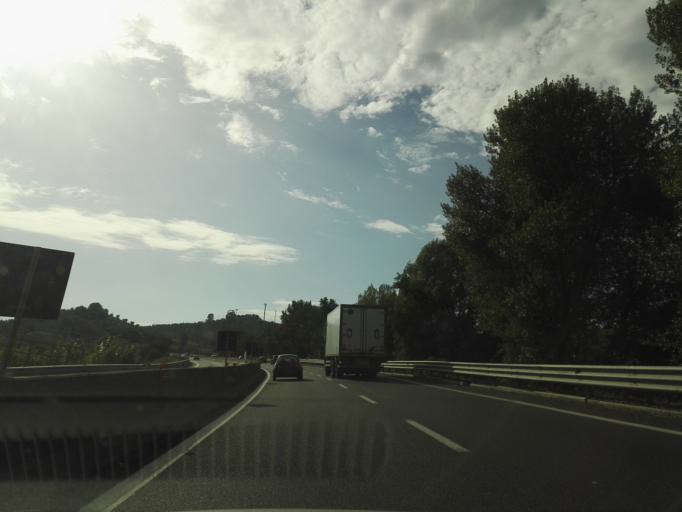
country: IT
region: Calabria
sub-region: Provincia di Catanzaro
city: Marcellinara
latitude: 38.9170
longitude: 16.4892
